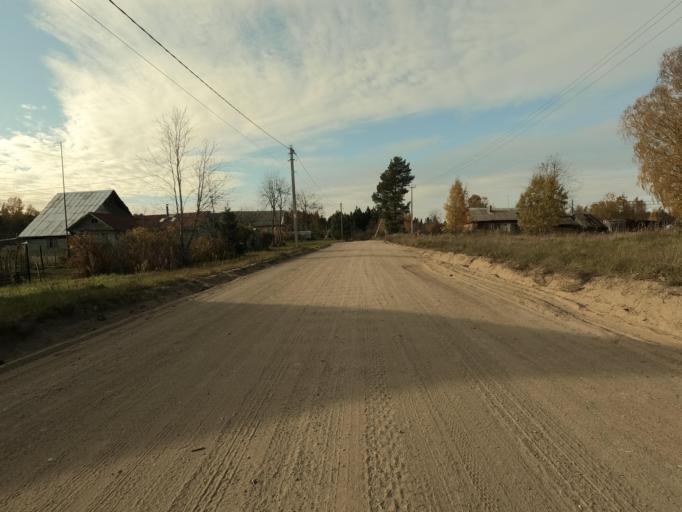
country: RU
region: Leningrad
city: Priladozhskiy
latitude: 59.6305
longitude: 31.4007
